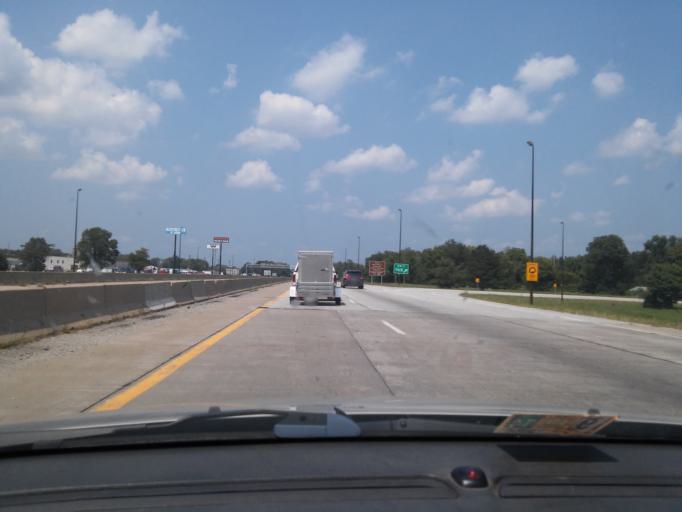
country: US
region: Illinois
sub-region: Sangamon County
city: Grandview
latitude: 39.7867
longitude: -89.5992
